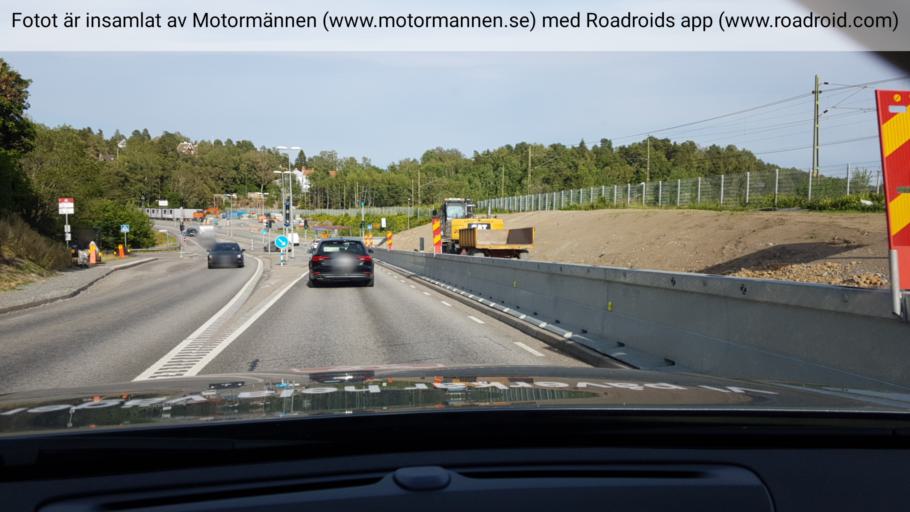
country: SE
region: Stockholm
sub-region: Botkyrka Kommun
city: Tullinge
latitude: 59.1997
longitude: 17.8812
